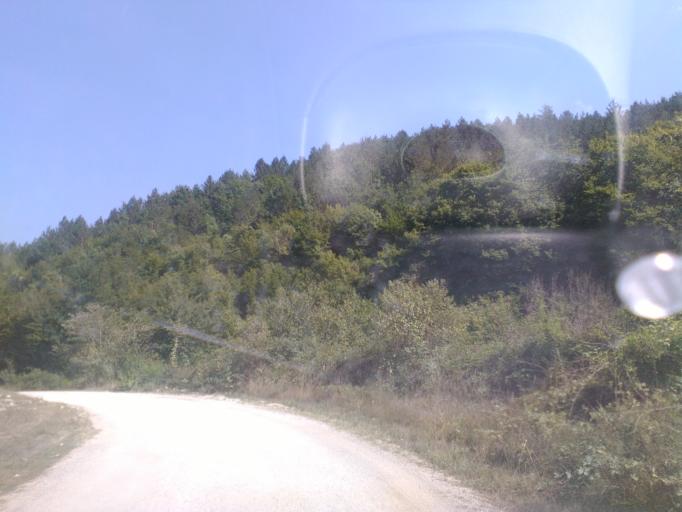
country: BA
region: Federation of Bosnia and Herzegovina
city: Orasac
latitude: 44.6207
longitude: 16.0621
